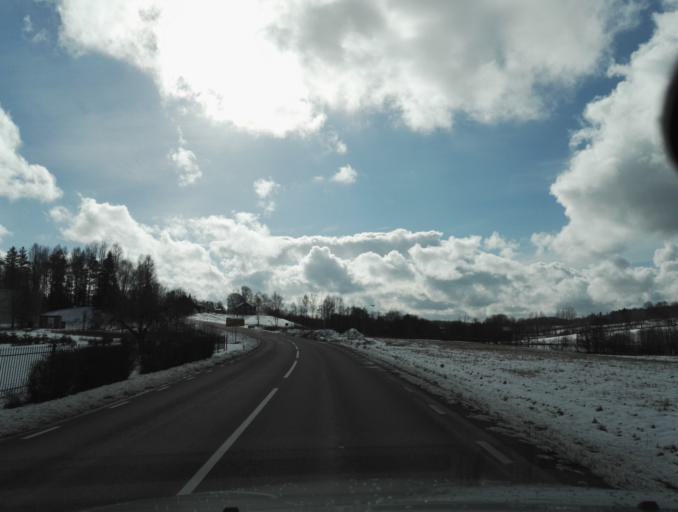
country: SE
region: Vaestra Goetaland
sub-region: Bollebygds Kommun
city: Bollebygd
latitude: 57.6838
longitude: 12.5650
